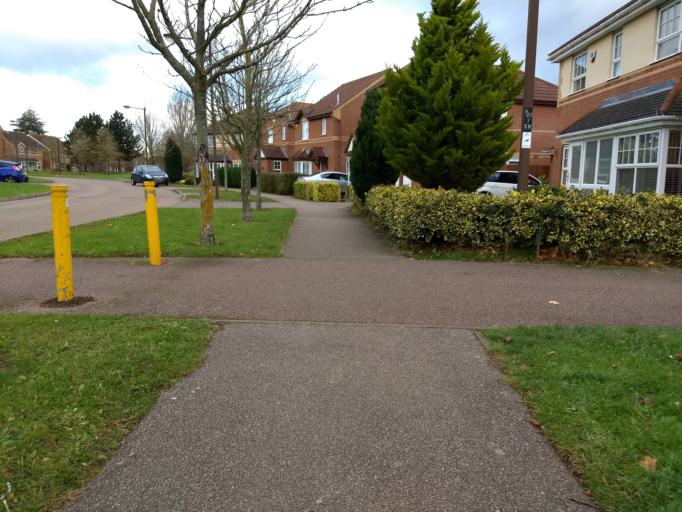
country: GB
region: England
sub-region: Milton Keynes
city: Shenley Church End
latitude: 52.0048
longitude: -0.7786
